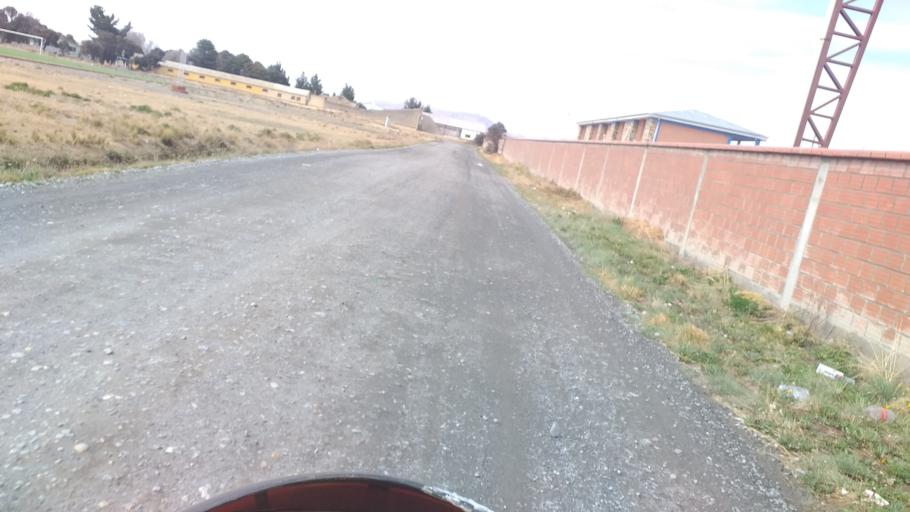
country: BO
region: La Paz
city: Achacachi
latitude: -16.0177
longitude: -68.7015
